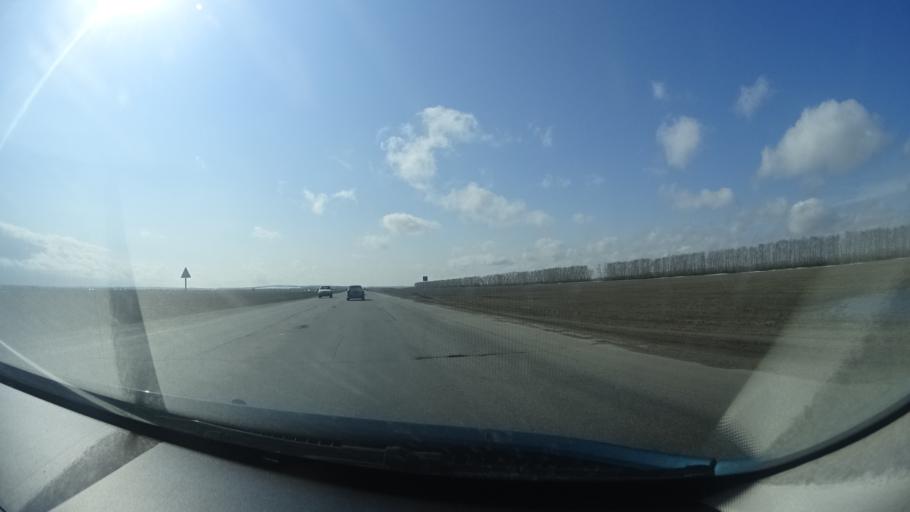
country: RU
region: Bashkortostan
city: Mikhaylovka
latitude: 54.9459
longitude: 55.7507
